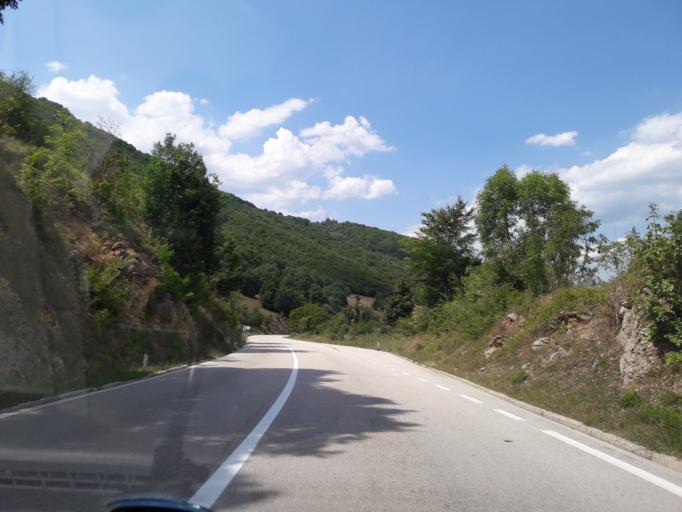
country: BA
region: Republika Srpska
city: Mrkonjic Grad
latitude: 44.5139
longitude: 17.1525
